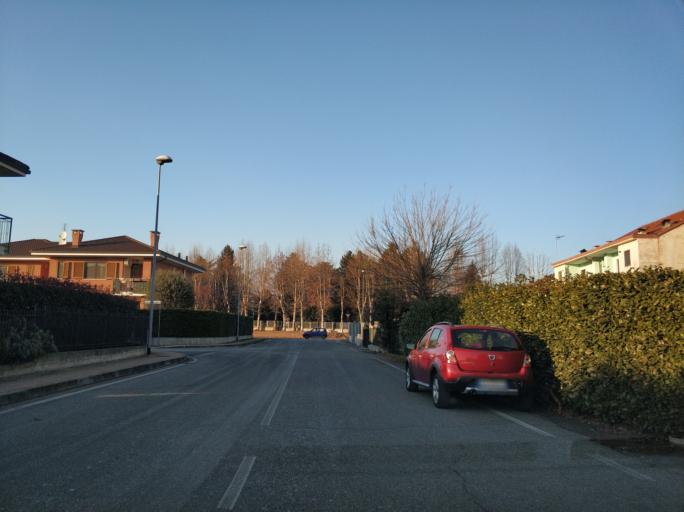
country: IT
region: Piedmont
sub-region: Provincia di Torino
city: San Maurizio
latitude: 45.2065
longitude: 7.6354
